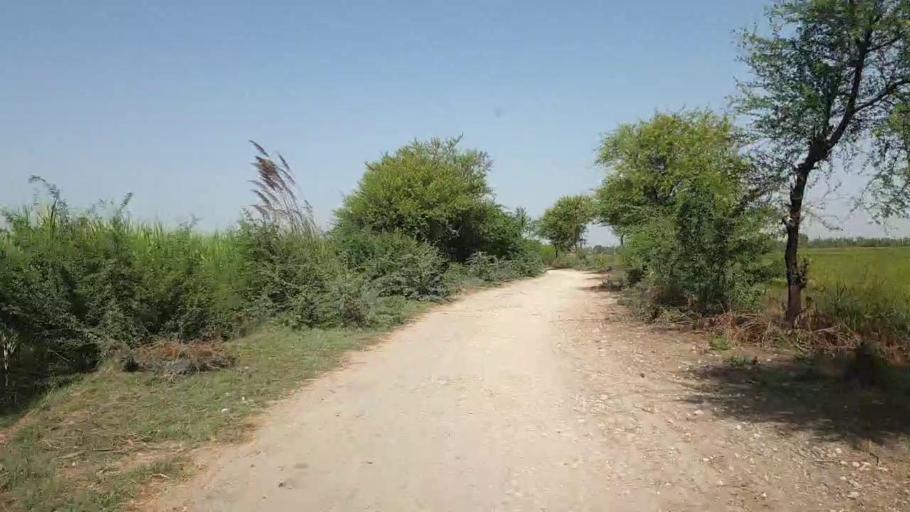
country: PK
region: Sindh
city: Tando Bago
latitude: 24.7584
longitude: 69.0244
